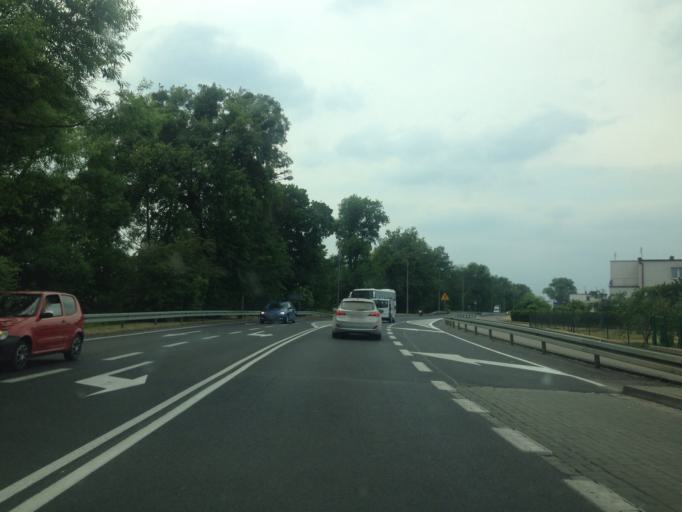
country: PL
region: Kujawsko-Pomorskie
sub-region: Powiat grudziadzki
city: Rogozno
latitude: 53.5025
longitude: 18.8446
